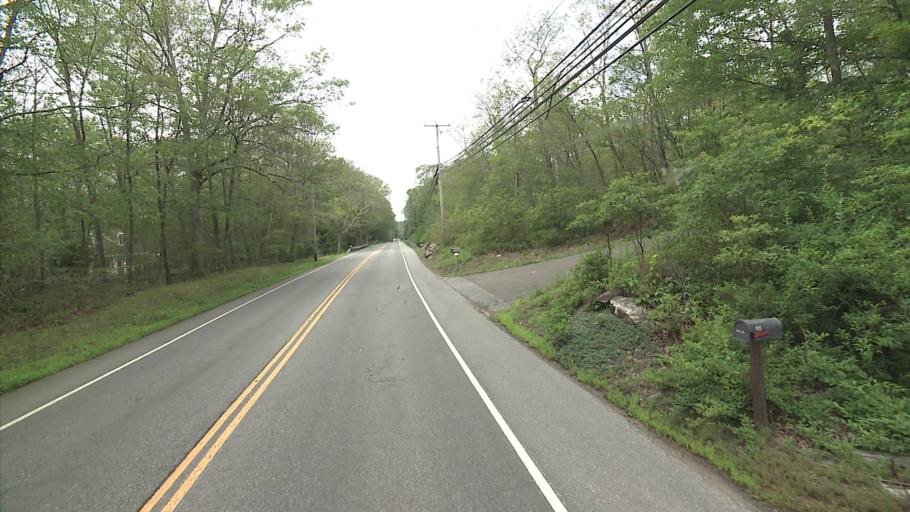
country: US
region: Connecticut
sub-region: New Haven County
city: Guilford
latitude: 41.3505
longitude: -72.6652
